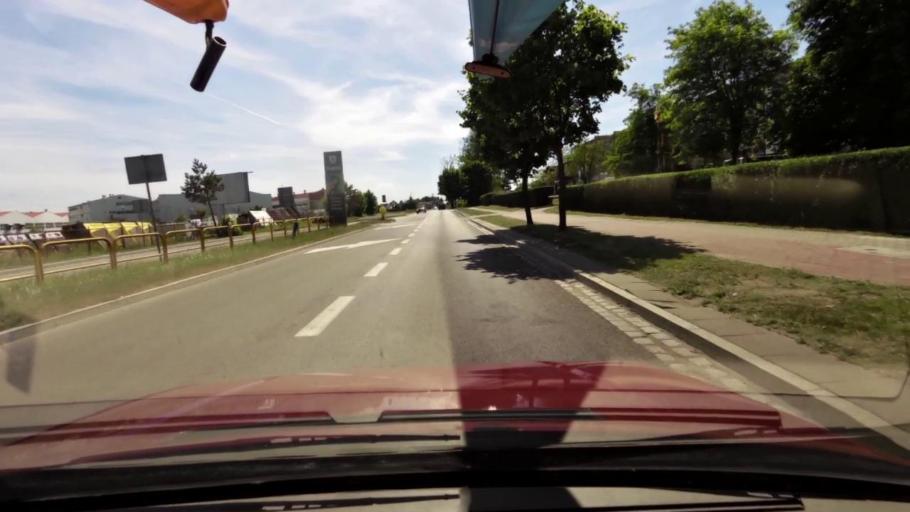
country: PL
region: Pomeranian Voivodeship
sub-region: Powiat slupski
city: Kobylnica
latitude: 54.4498
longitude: 17.0130
